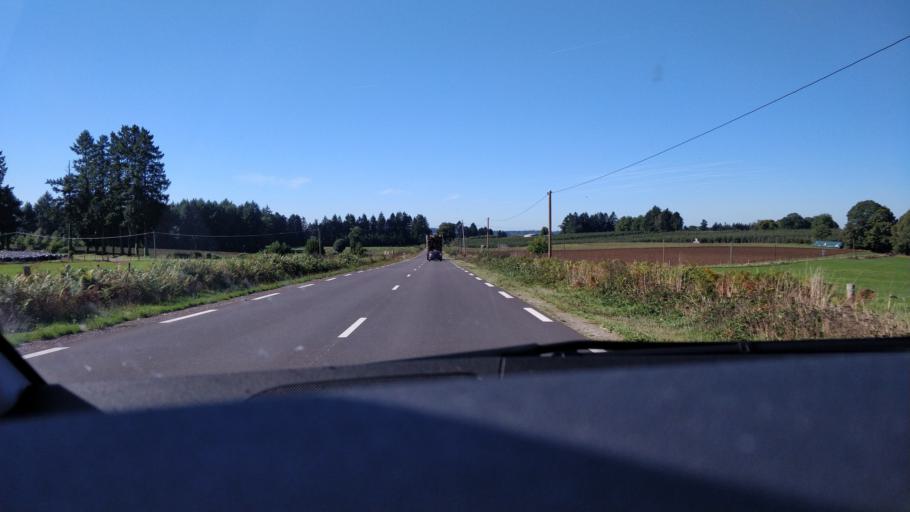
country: FR
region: Limousin
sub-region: Departement de la Haute-Vienne
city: Saint-Leonard-de-Noblat
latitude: 45.8700
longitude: 1.5322
